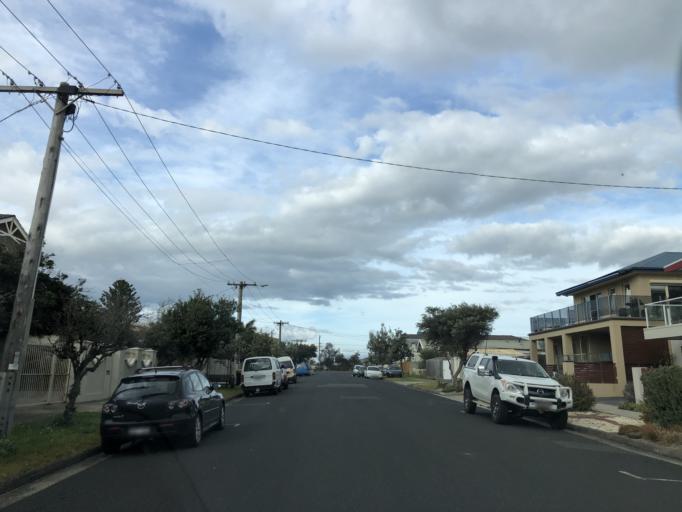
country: AU
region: Victoria
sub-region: Kingston
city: Bonbeach
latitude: -38.0609
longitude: 145.1173
